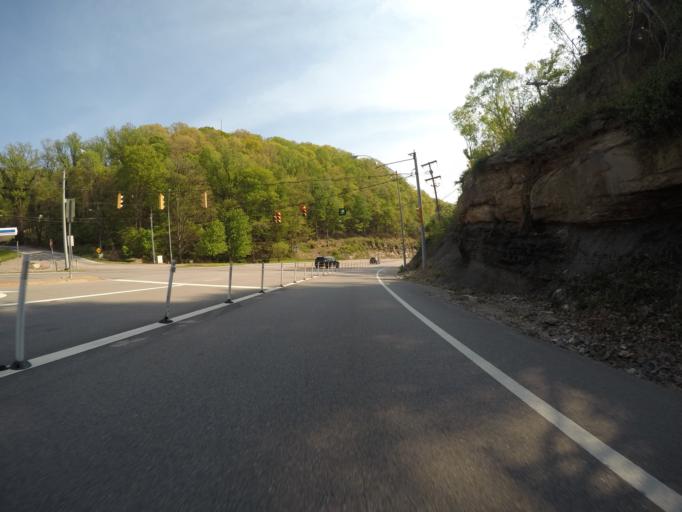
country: US
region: West Virginia
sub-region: Kanawha County
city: Charleston
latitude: 38.3470
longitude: -81.6054
